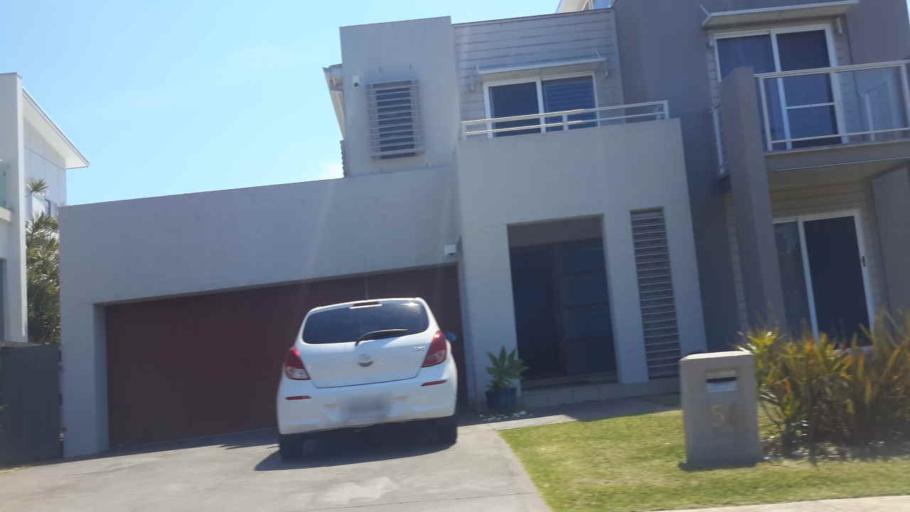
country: AU
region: New South Wales
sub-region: Wollongong
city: Bulli
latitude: -34.3273
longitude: 150.9214
